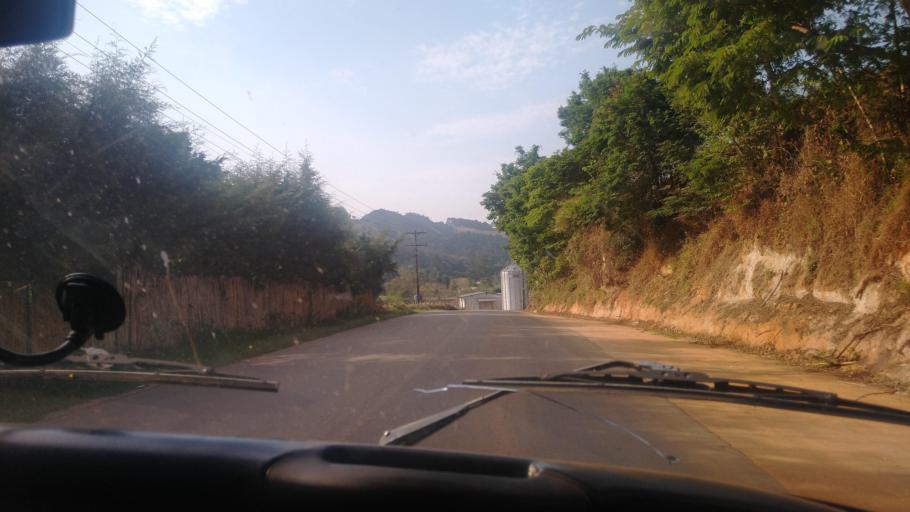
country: BR
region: Minas Gerais
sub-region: Extrema
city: Extrema
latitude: -22.7834
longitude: -46.4427
